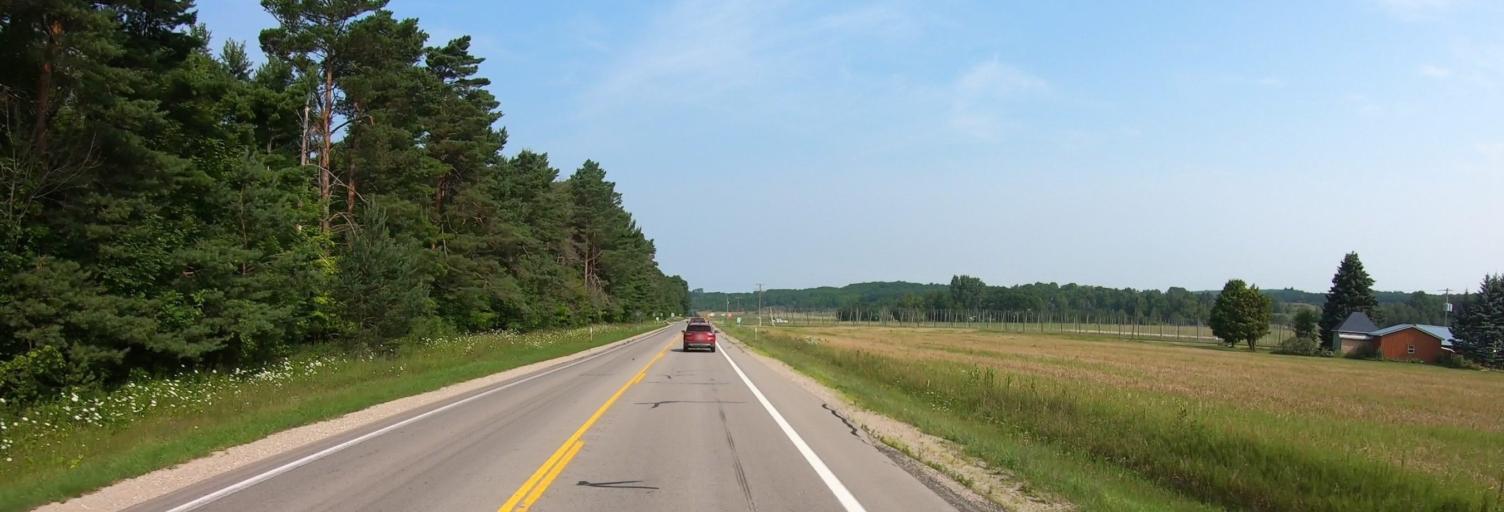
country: US
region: Michigan
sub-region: Benzie County
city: Beulah
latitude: 44.8065
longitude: -86.0172
